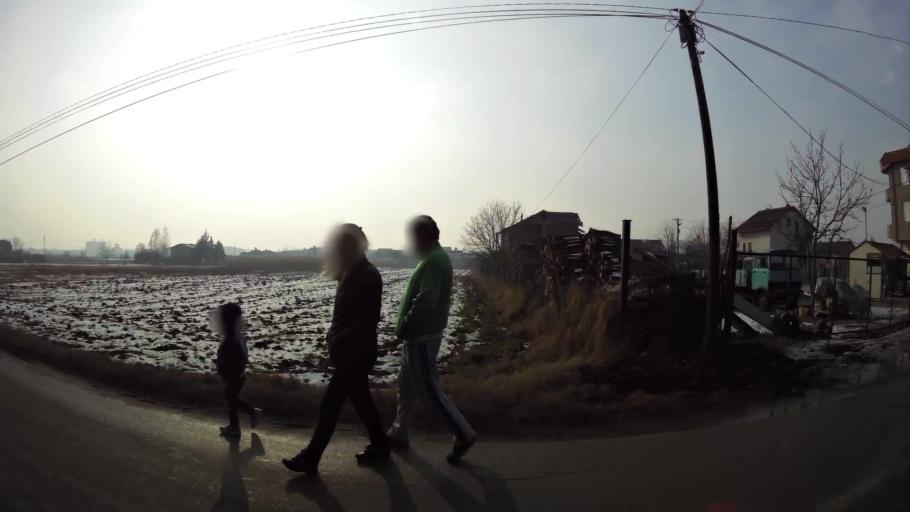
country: MK
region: Ilinden
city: Marino
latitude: 41.9817
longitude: 21.5965
